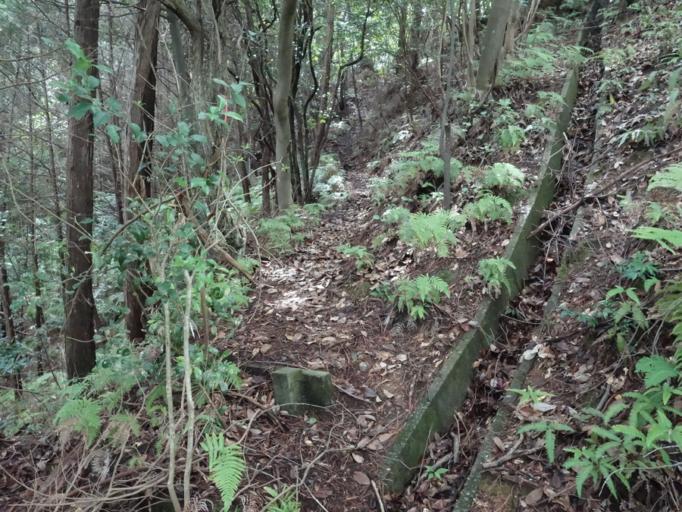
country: JP
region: Yamaguchi
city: Yamaguchi-shi
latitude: 34.1439
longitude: 131.4735
